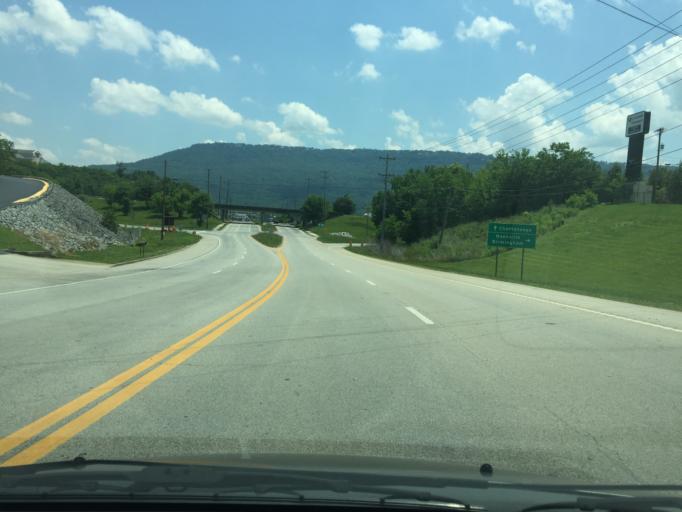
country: US
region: Tennessee
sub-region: Hamilton County
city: Lookout Mountain
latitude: 35.0194
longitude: -85.3859
